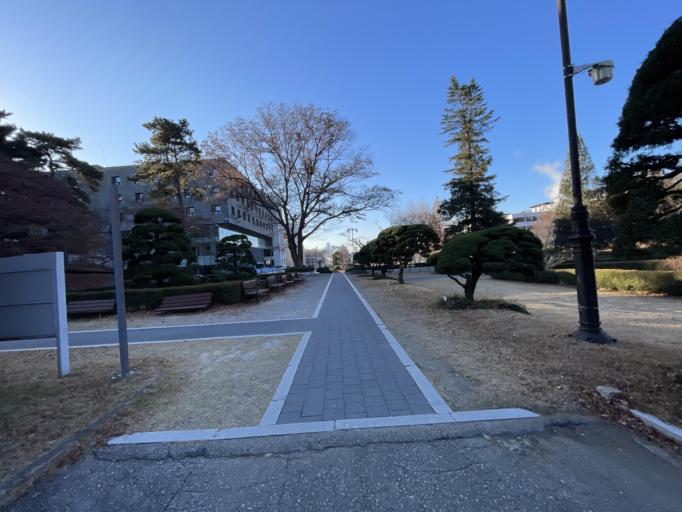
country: KR
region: Seoul
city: Seoul
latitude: 37.5658
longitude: 126.9389
